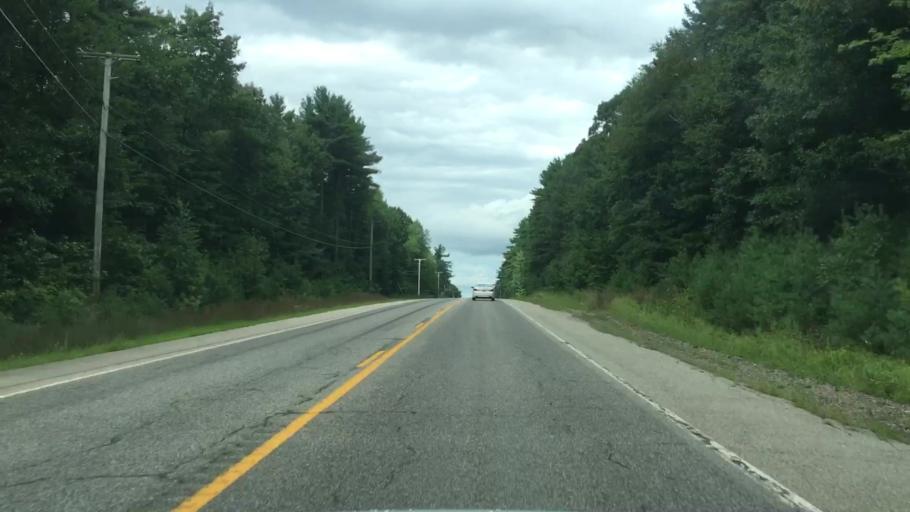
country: US
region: Maine
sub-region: York County
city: South Sanford
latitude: 43.3645
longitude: -70.7309
